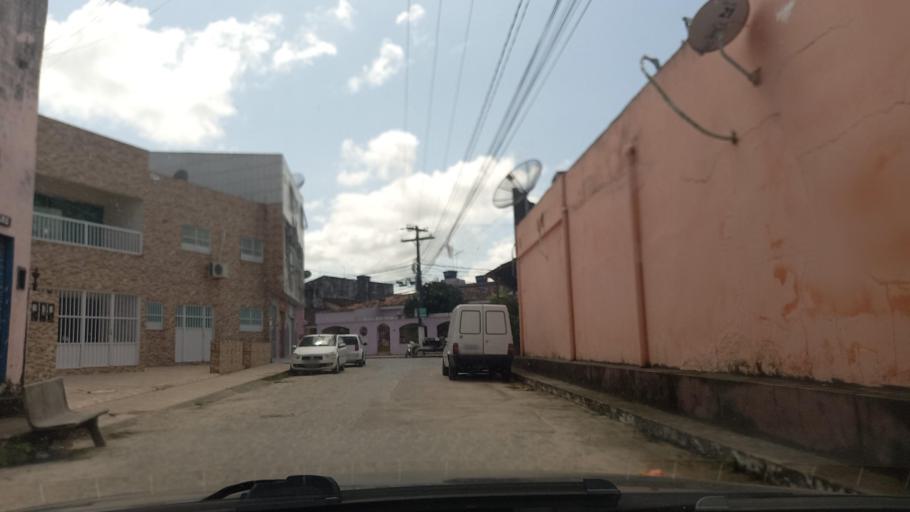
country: BR
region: Pernambuco
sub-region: Goiana
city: Goiana
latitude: -7.5606
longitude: -34.9947
